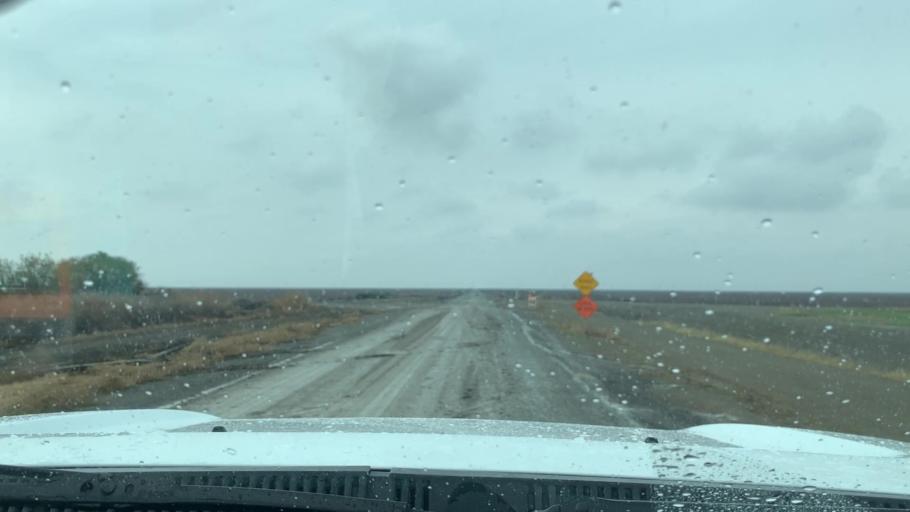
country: US
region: California
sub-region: Kings County
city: Corcoran
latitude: 36.0072
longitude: -119.5531
